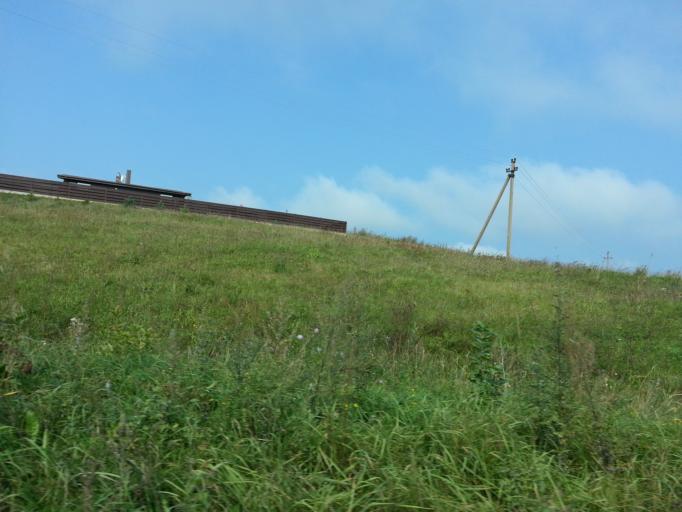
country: LT
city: Grigiskes
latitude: 54.7677
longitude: 25.0487
